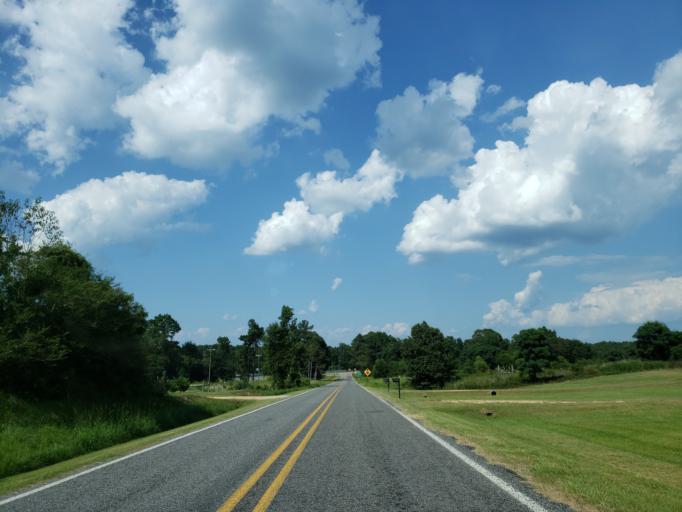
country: US
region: Mississippi
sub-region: Covington County
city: Collins
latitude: 31.6111
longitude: -89.4311
